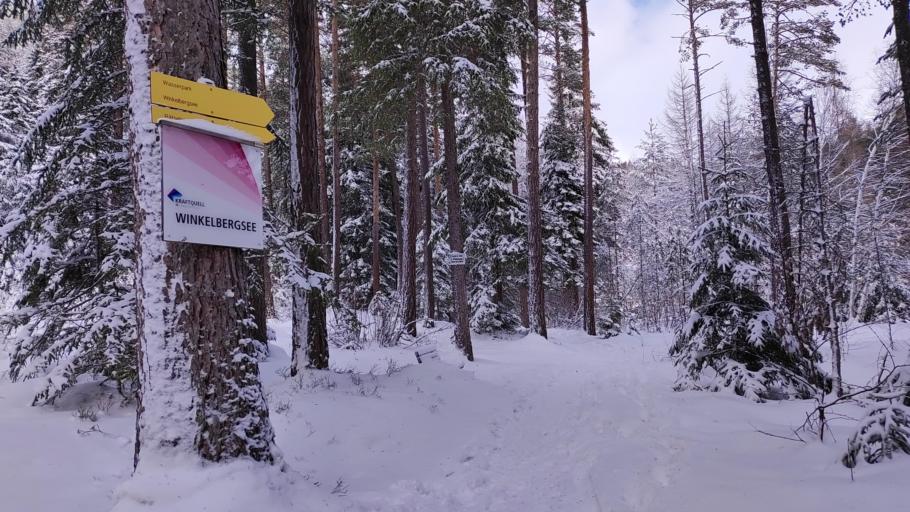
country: AT
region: Tyrol
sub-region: Politischer Bezirk Imst
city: Umhausen
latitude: 47.1022
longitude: 10.9334
